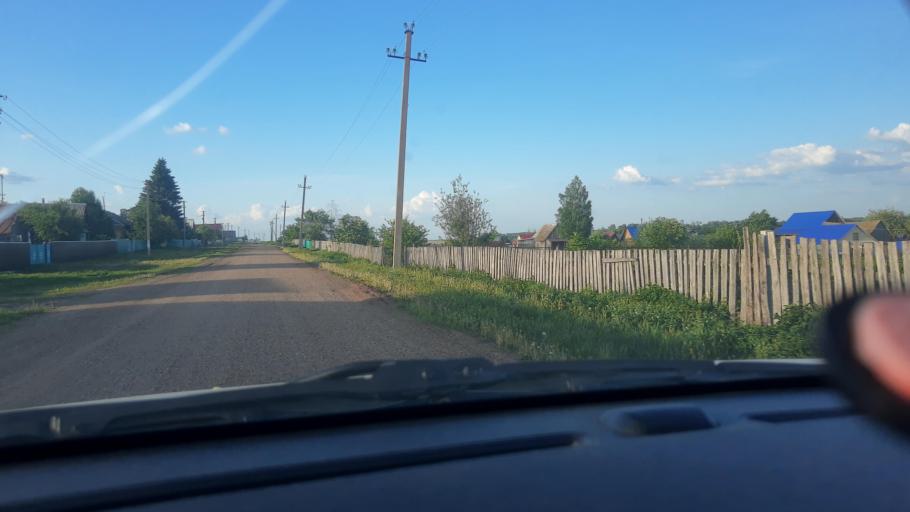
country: RU
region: Bashkortostan
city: Karmaskaly
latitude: 54.3808
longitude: 55.9385
